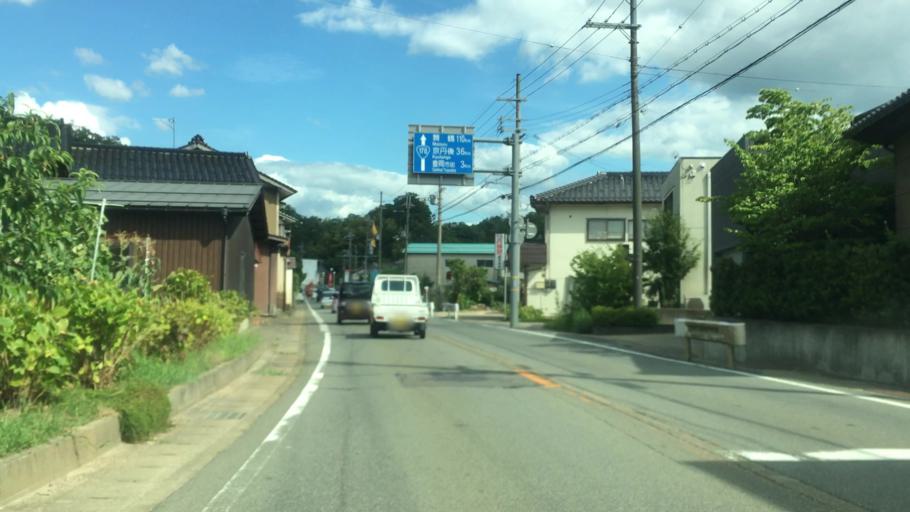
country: JP
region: Hyogo
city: Toyooka
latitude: 35.5549
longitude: 134.7981
